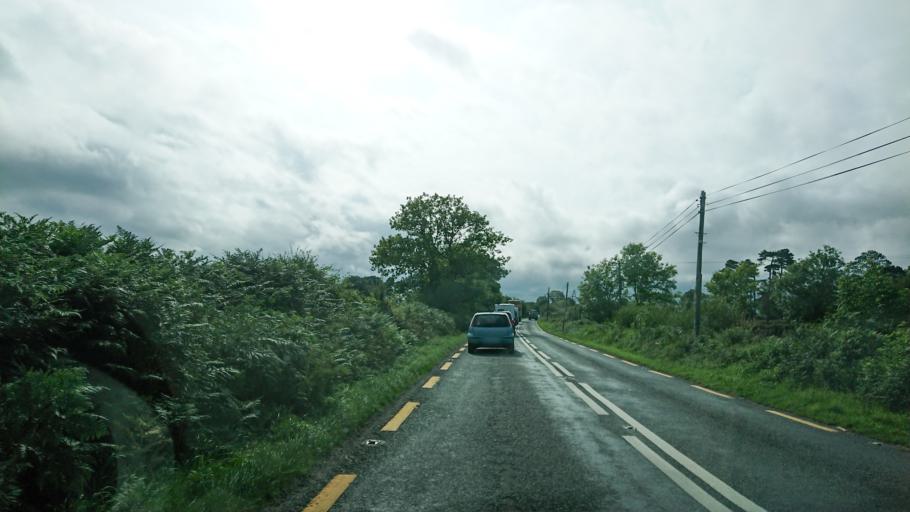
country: IE
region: Munster
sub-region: County Cork
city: Millstreet
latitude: 52.0849
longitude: -9.1804
